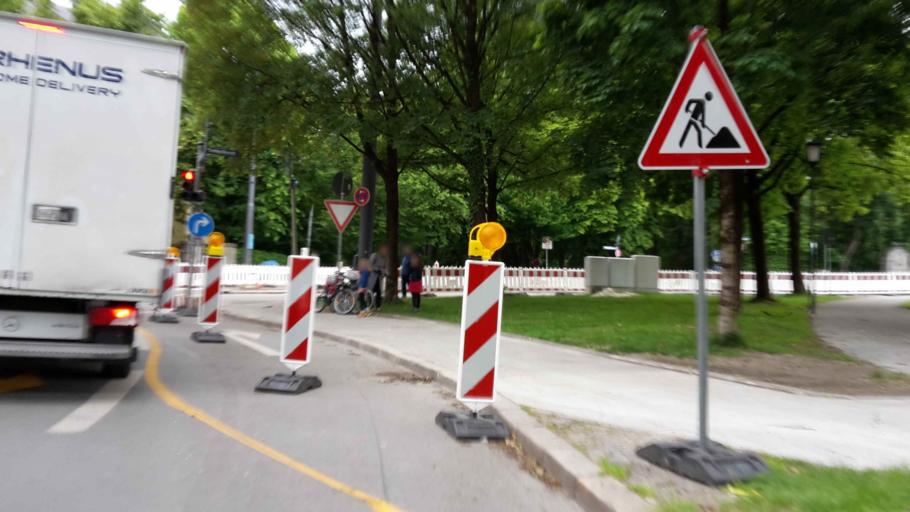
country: DE
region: Bavaria
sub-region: Upper Bavaria
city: Bogenhausen
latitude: 48.1492
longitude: 11.5998
